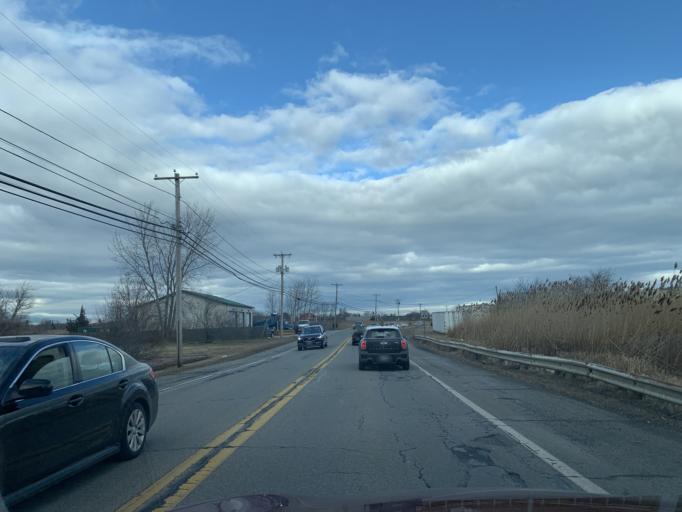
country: US
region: Massachusetts
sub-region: Essex County
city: Salisbury
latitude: 42.8289
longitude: -70.8648
